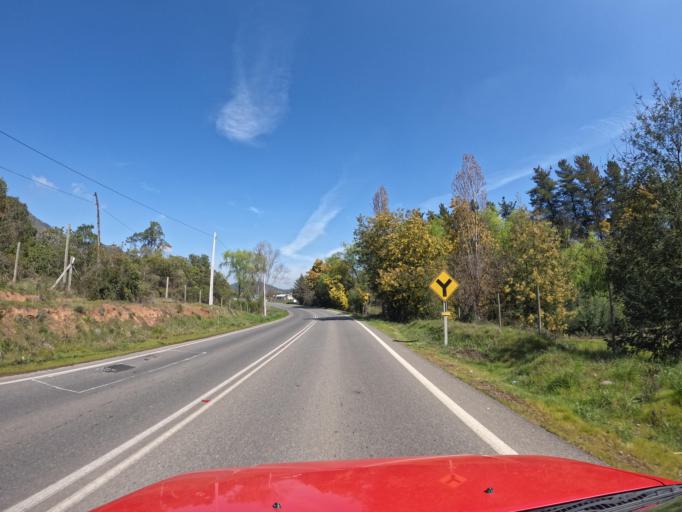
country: CL
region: Maule
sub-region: Provincia de Talca
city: San Clemente
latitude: -35.4821
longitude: -71.2708
